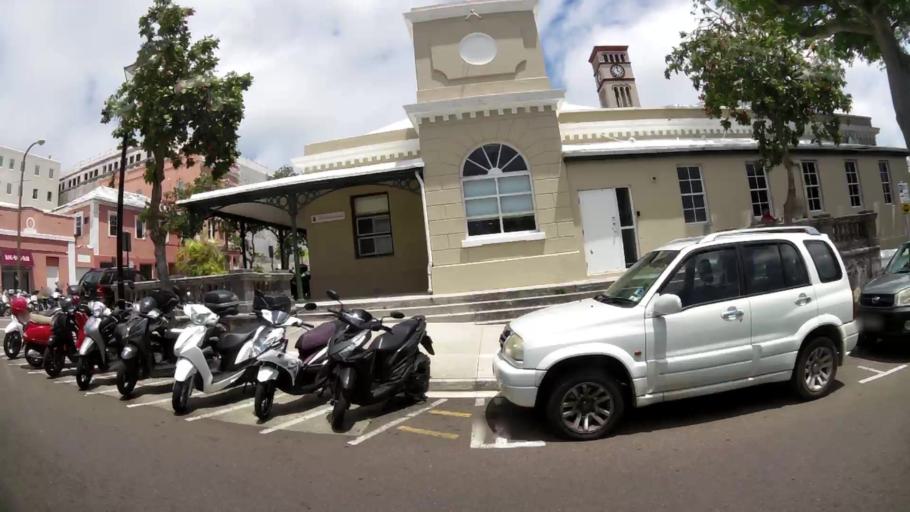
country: BM
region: Hamilton city
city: Hamilton
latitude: 32.2933
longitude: -64.7818
